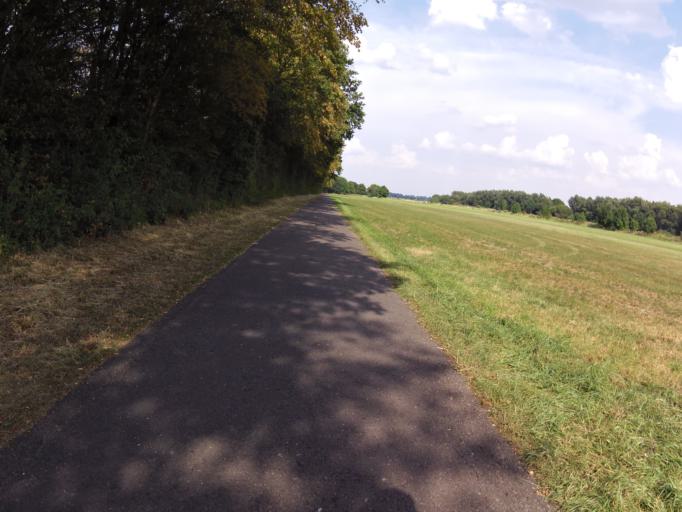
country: DE
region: North Rhine-Westphalia
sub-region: Regierungsbezirk Detmold
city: Petershagen
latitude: 52.3485
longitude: 8.9518
